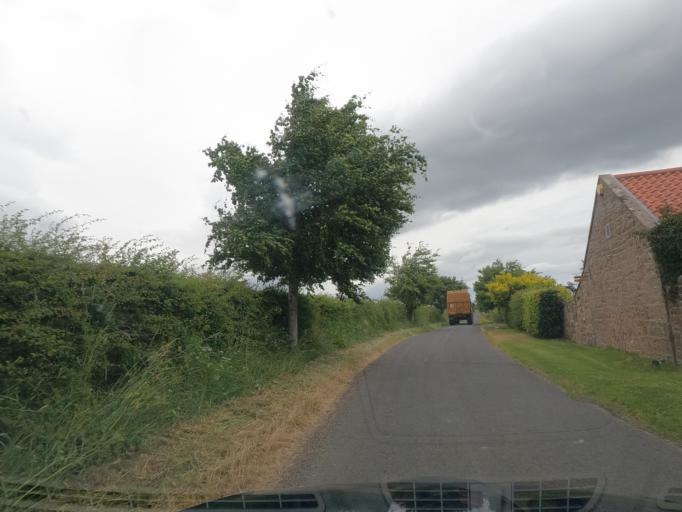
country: GB
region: England
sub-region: Northumberland
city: Lowick
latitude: 55.5752
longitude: -1.9199
